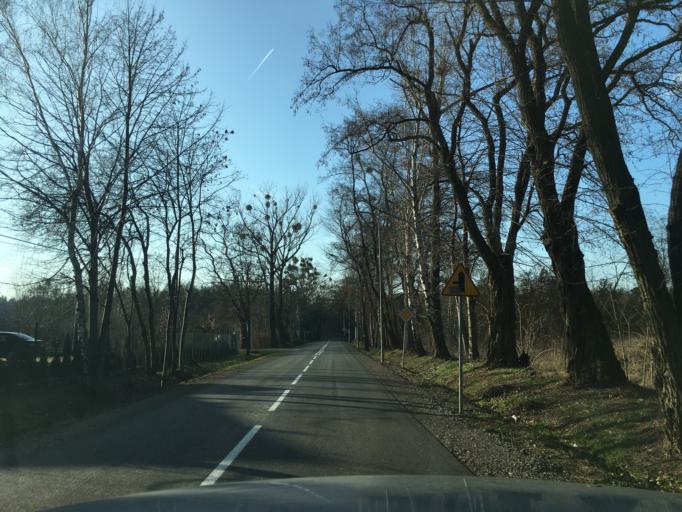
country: PL
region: Lodz Voivodeship
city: Zabia Wola
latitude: 52.0488
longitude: 20.7435
